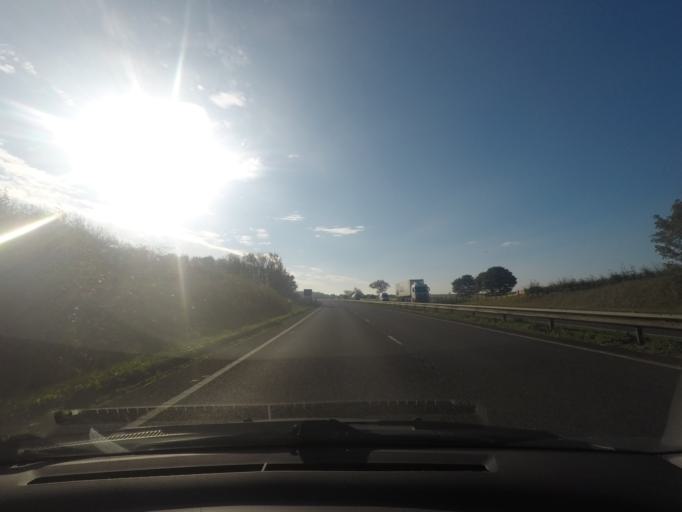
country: GB
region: England
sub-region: North Lincolnshire
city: Barton upon Humber
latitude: 53.6479
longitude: -0.4513
